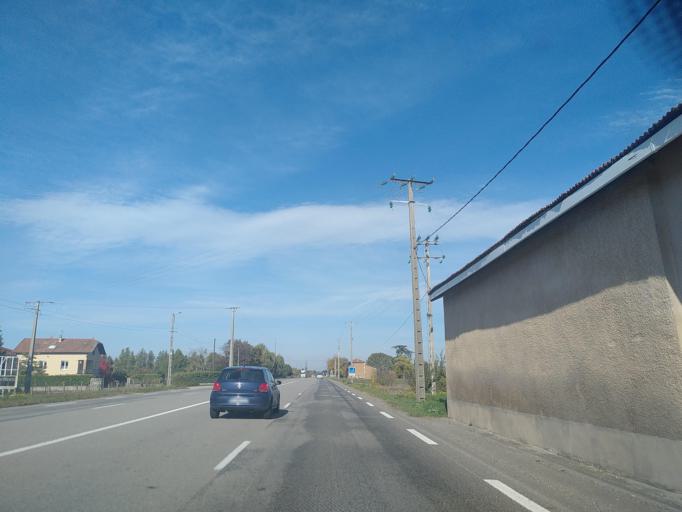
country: FR
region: Rhone-Alpes
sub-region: Departement de la Drome
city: Andancette
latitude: 45.2460
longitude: 4.8209
